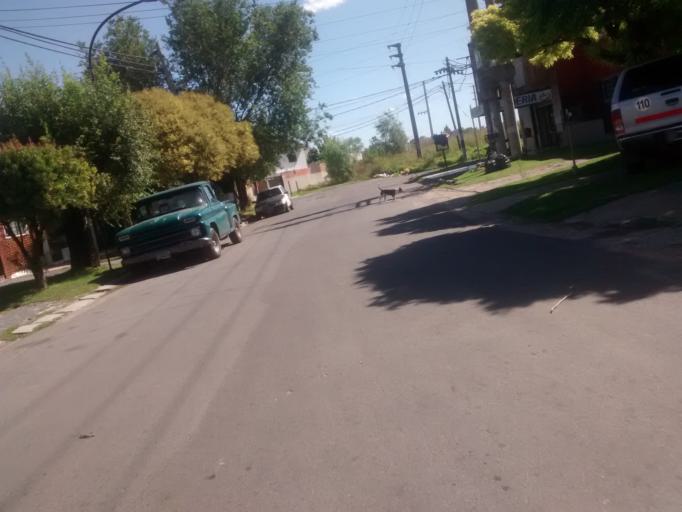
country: AR
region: Buenos Aires
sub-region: Partido de La Plata
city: La Plata
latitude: -34.9329
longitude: -57.9055
